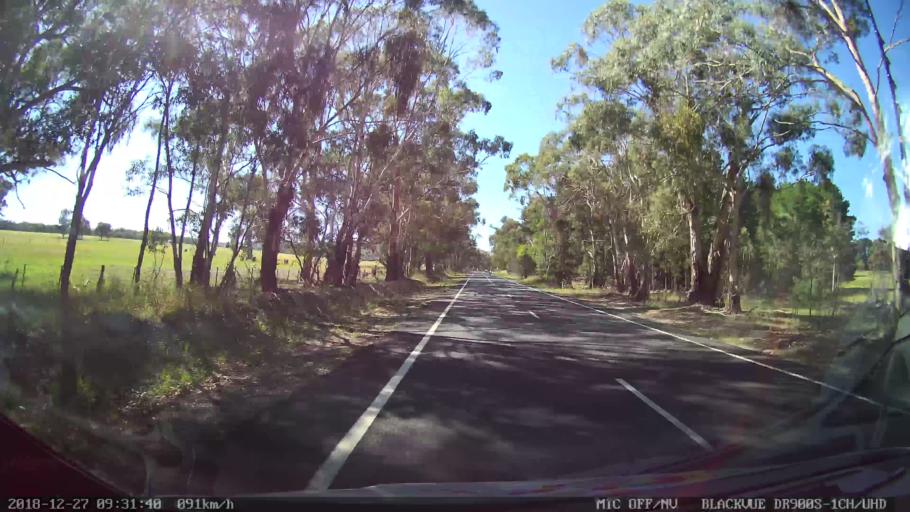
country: AU
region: New South Wales
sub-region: Lithgow
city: Portland
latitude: -33.1969
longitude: 150.0114
